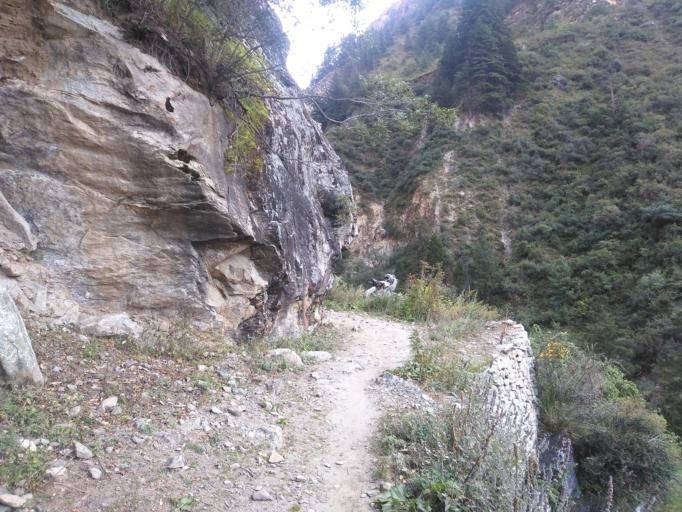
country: NP
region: Western Region
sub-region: Dhawalagiri Zone
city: Jomsom
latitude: 28.9178
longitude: 83.0310
